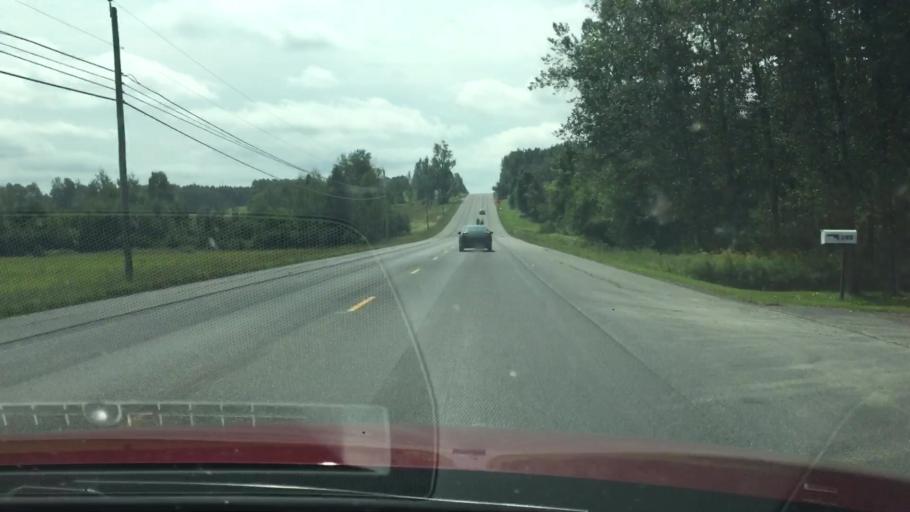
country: US
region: Maine
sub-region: Aroostook County
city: Houlton
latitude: 46.3581
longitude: -67.8423
